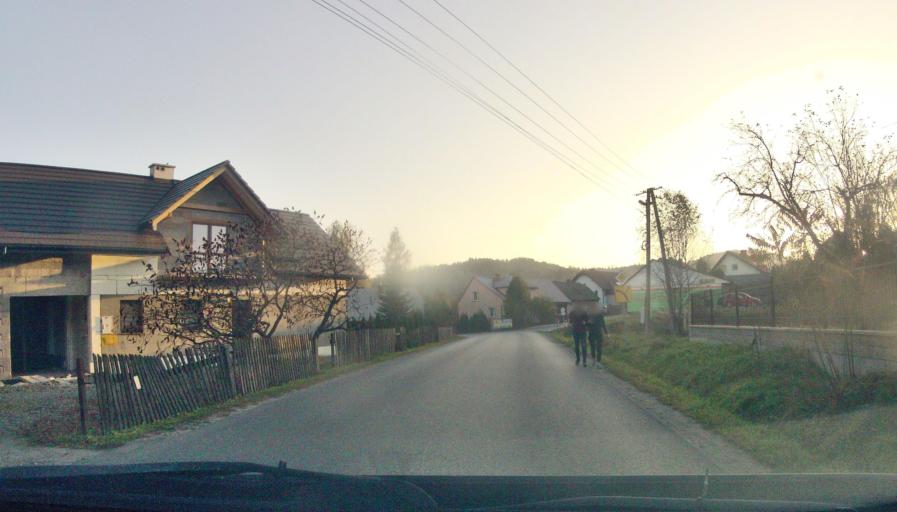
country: PL
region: Lesser Poland Voivodeship
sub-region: Powiat suski
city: Kukow
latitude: 49.7458
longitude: 19.4663
